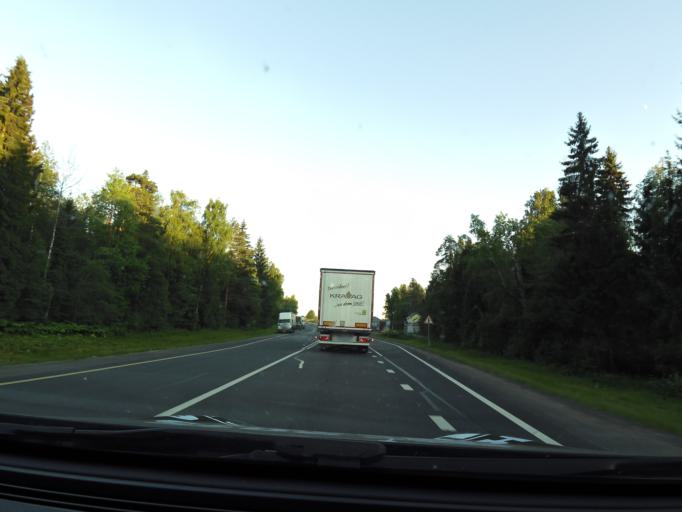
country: RU
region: Jaroslavl
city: Prechistoye
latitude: 58.4383
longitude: 40.3213
